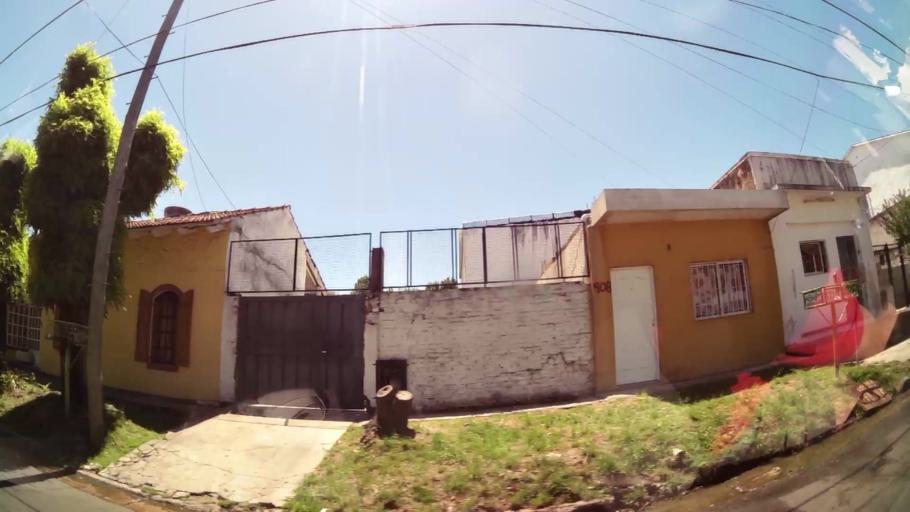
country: AR
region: Buenos Aires
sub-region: Partido de Tigre
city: Tigre
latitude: -34.4893
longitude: -58.6357
